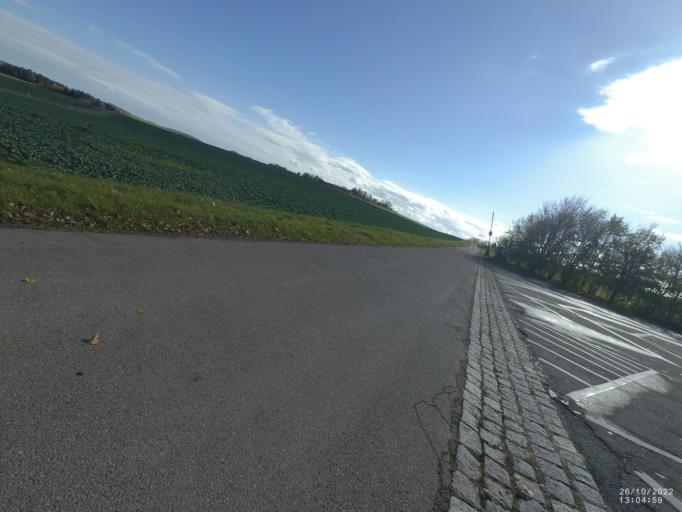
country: DE
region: Baden-Wuerttemberg
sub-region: Regierungsbezirk Stuttgart
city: Donzdorf
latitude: 48.6812
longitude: 9.8411
